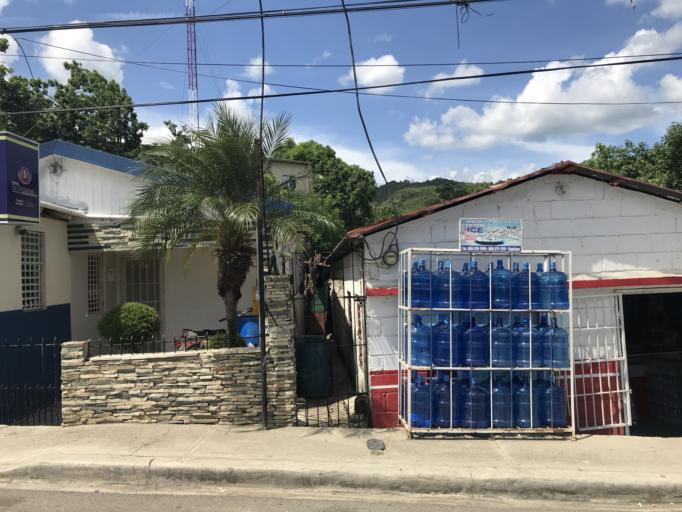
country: DO
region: Santiago
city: Tamboril
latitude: 19.5034
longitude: -70.6518
